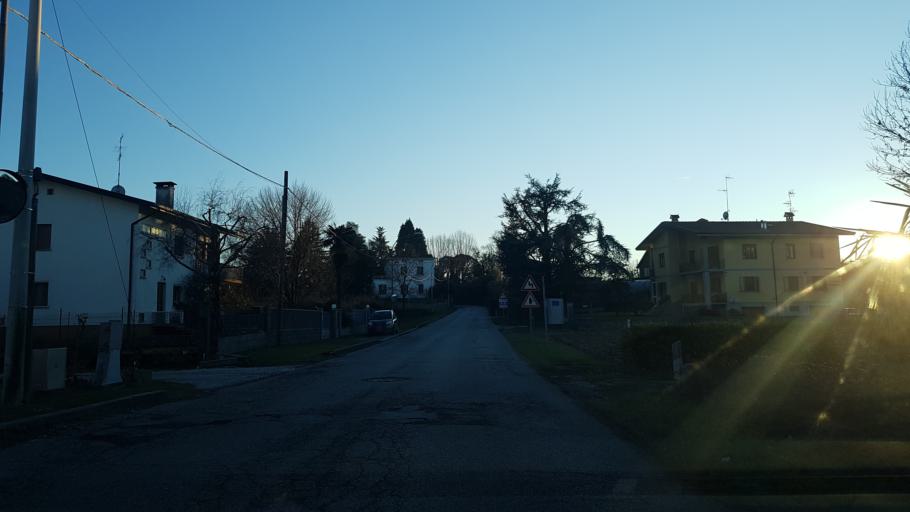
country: IT
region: Friuli Venezia Giulia
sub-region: Provincia di Udine
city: Tricesimo
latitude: 46.1717
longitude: 13.2170
